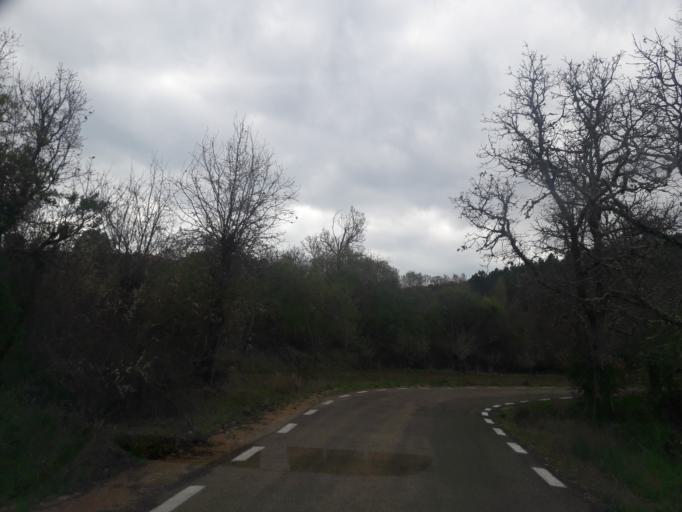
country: ES
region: Castille and Leon
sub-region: Provincia de Salamanca
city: Serradilla del Arroyo
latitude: 40.5137
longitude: -6.3916
